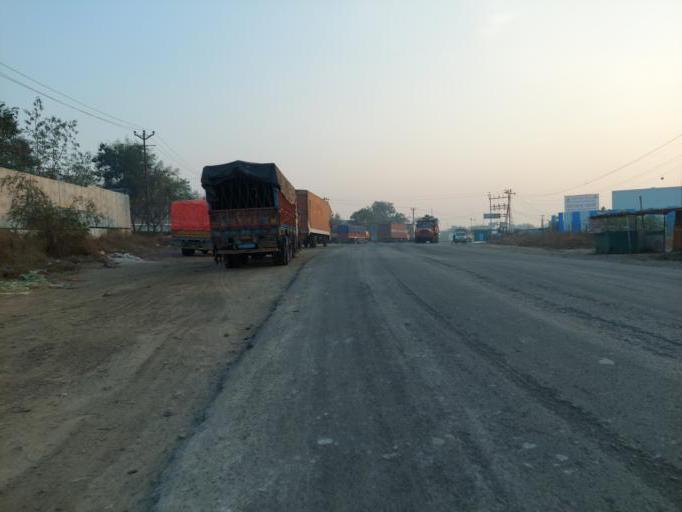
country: IN
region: Maharashtra
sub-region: Pune Division
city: Pune
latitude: 18.4662
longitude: 73.9551
